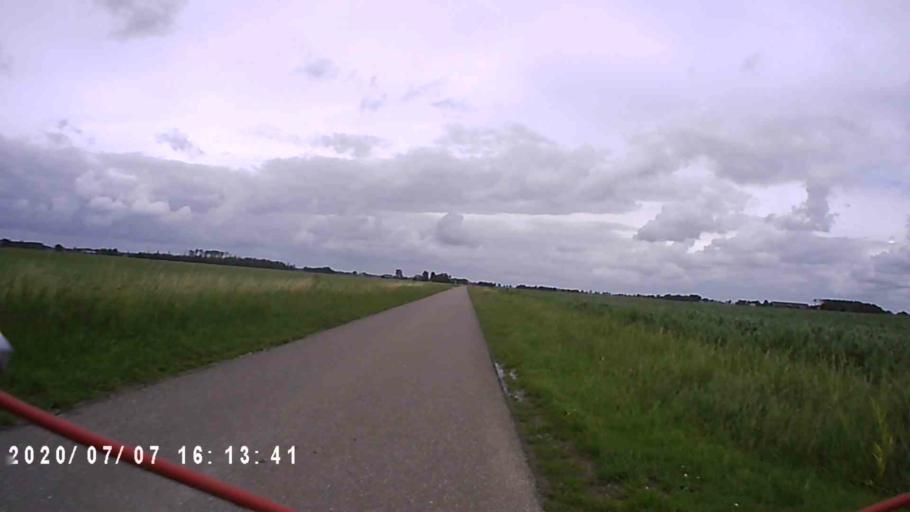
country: NL
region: Groningen
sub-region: Gemeente Winsum
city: Winsum
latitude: 53.3721
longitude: 6.5395
